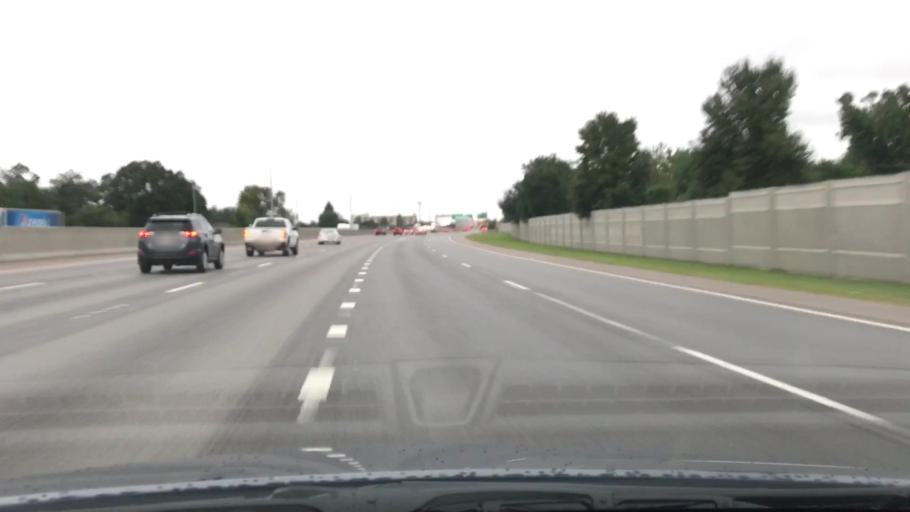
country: US
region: Louisiana
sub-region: Jefferson Parish
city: Kenner
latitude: 30.0013
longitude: -90.2021
